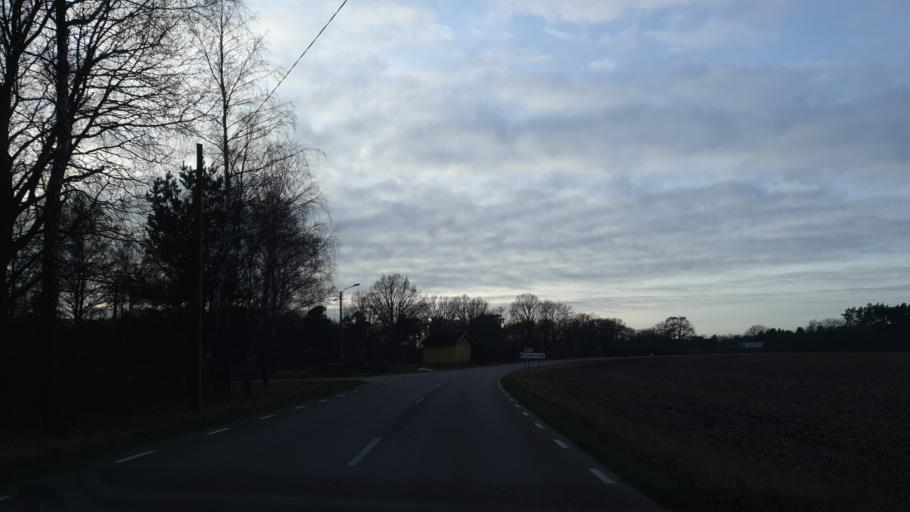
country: SE
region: Kalmar
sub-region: Torsas Kommun
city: Torsas
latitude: 56.2534
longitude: 16.0237
